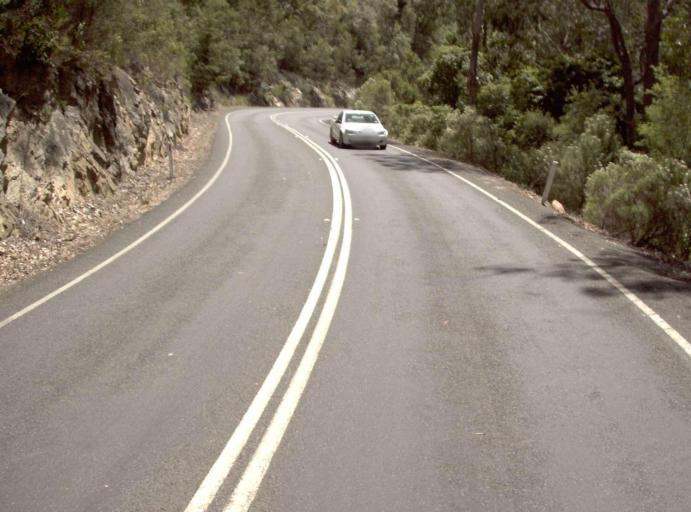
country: AU
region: Victoria
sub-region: East Gippsland
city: Lakes Entrance
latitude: -37.6187
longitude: 147.8814
